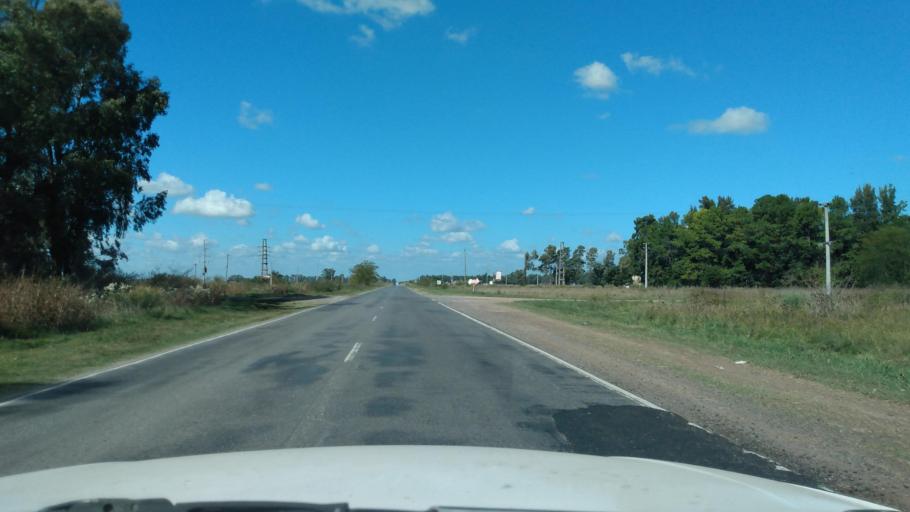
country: AR
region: Buenos Aires
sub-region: Partido de Mercedes
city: Mercedes
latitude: -34.7192
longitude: -59.3953
